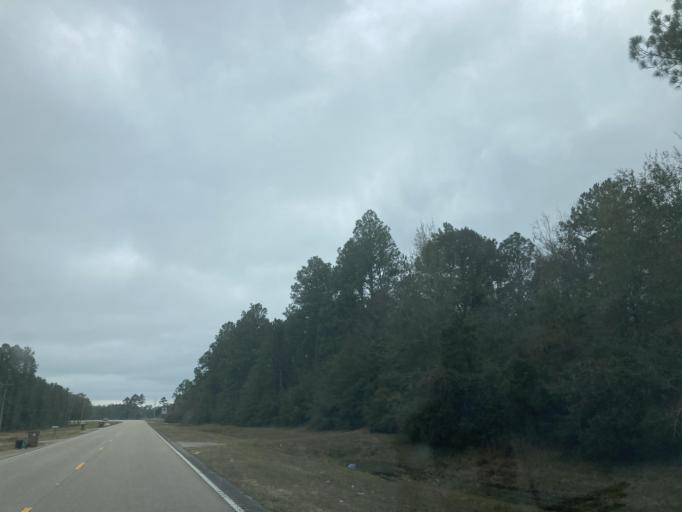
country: US
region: Mississippi
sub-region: Jackson County
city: Latimer
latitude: 30.5458
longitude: -88.9276
